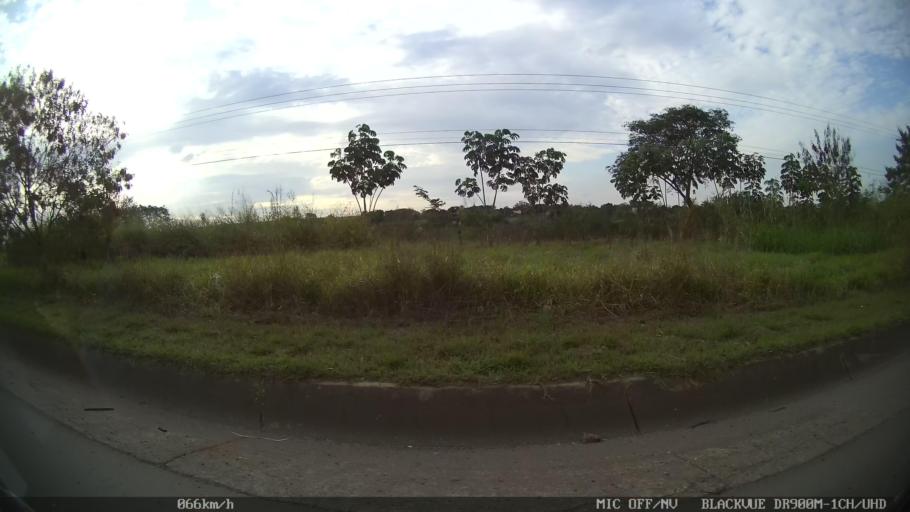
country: BR
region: Sao Paulo
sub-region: Cosmopolis
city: Cosmopolis
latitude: -22.6295
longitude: -47.2837
